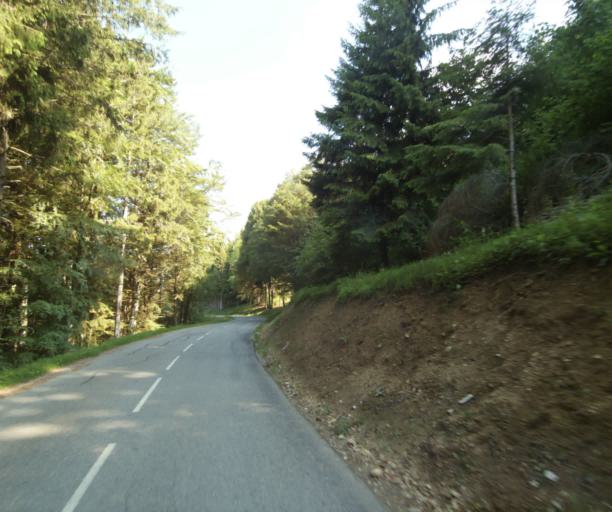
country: FR
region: Rhone-Alpes
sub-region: Departement de la Haute-Savoie
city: Lyaud
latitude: 46.2977
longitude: 6.5094
